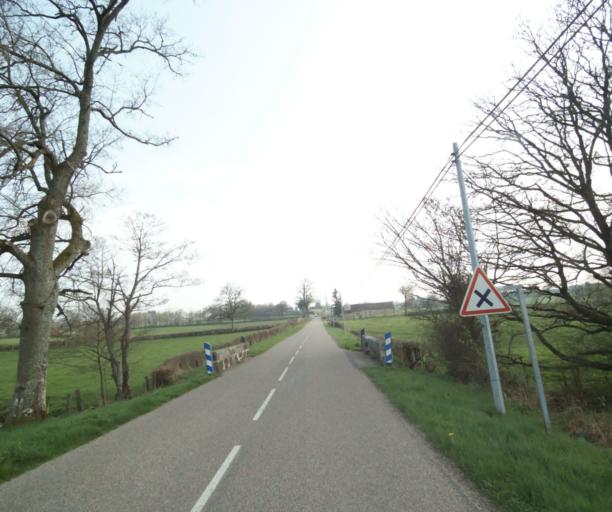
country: FR
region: Bourgogne
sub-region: Departement de Saone-et-Loire
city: Charolles
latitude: 46.4694
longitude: 4.4369
